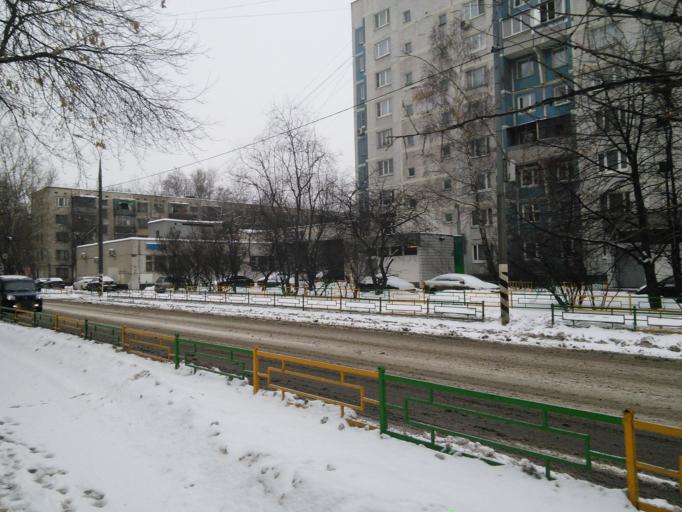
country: RU
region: Moscow
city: Lefortovo
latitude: 55.7714
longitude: 37.7121
